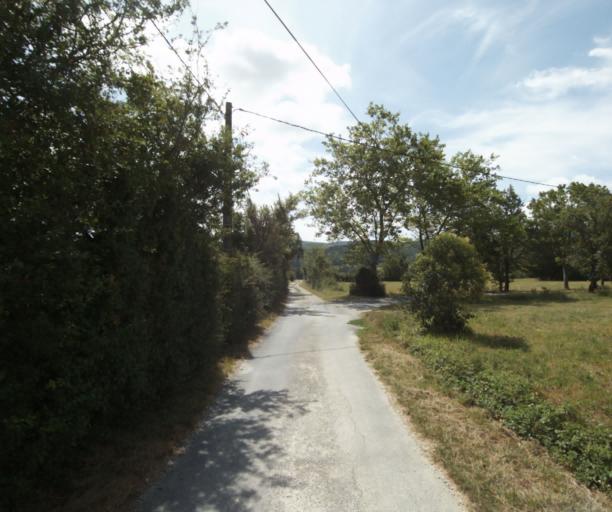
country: FR
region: Midi-Pyrenees
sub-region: Departement du Tarn
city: Dourgne
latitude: 43.4808
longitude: 2.1161
